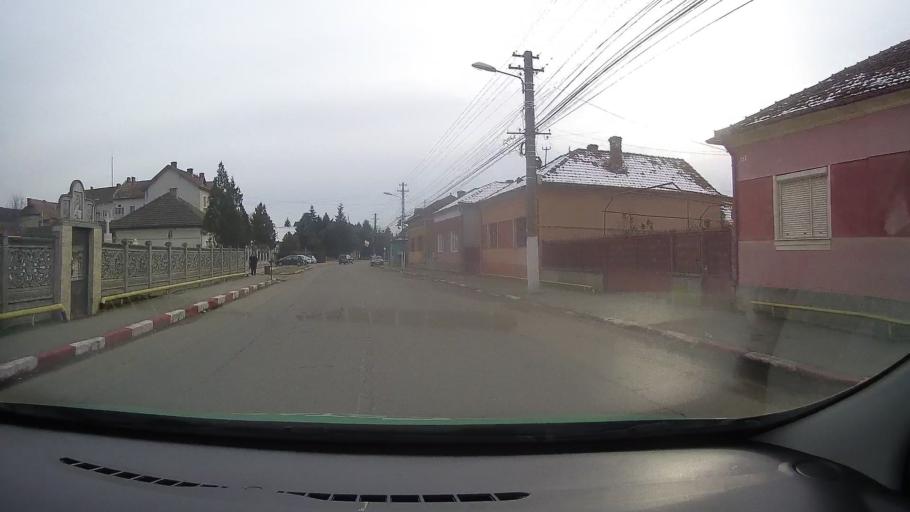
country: RO
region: Hunedoara
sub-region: Comuna Geoagiu
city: Geoagiu
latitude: 45.9221
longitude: 23.1993
